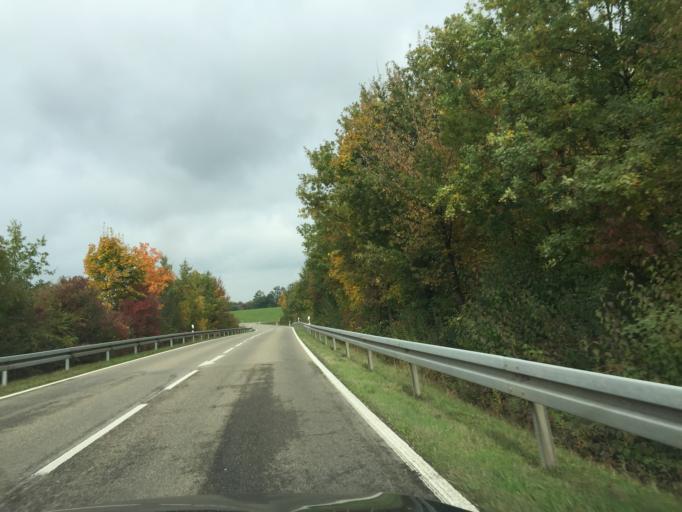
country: DE
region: Baden-Wuerttemberg
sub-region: Karlsruhe Region
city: Bretten
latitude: 49.0954
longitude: 8.7196
